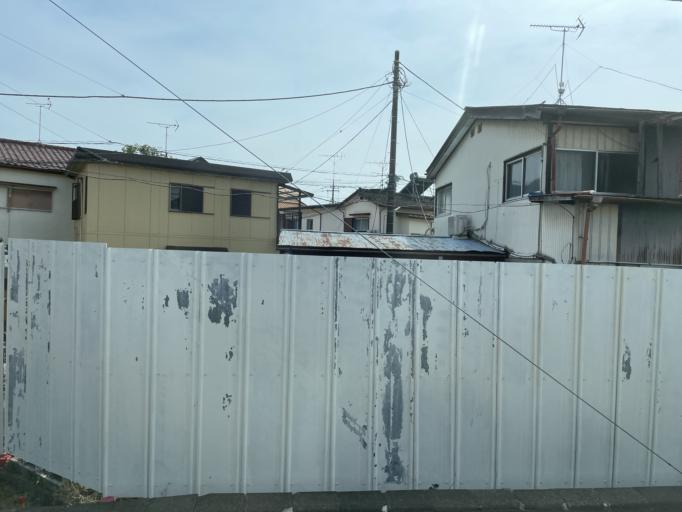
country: JP
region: Saitama
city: Hanno
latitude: 35.8396
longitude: 139.3476
